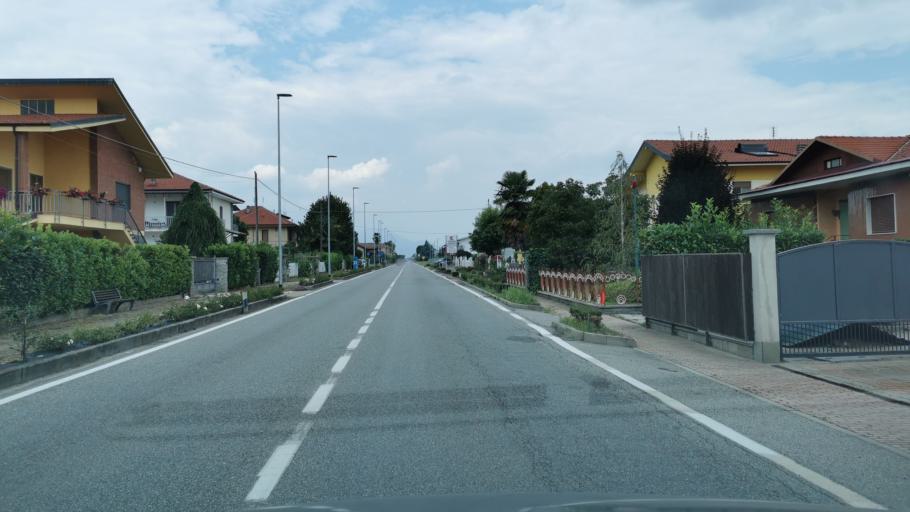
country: IT
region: Piedmont
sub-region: Provincia di Torino
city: Cavour
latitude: 44.7964
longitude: 7.3744
